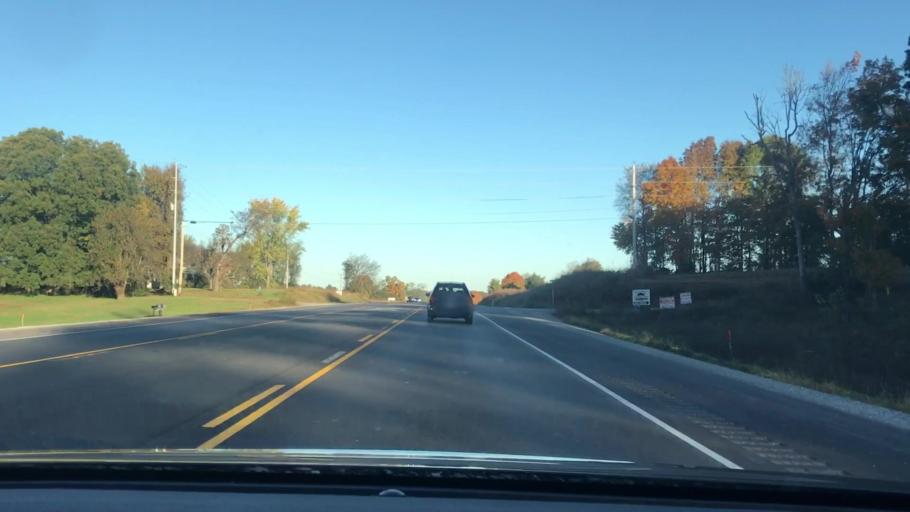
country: US
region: Kentucky
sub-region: Simpson County
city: Franklin
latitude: 36.6754
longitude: -86.5614
